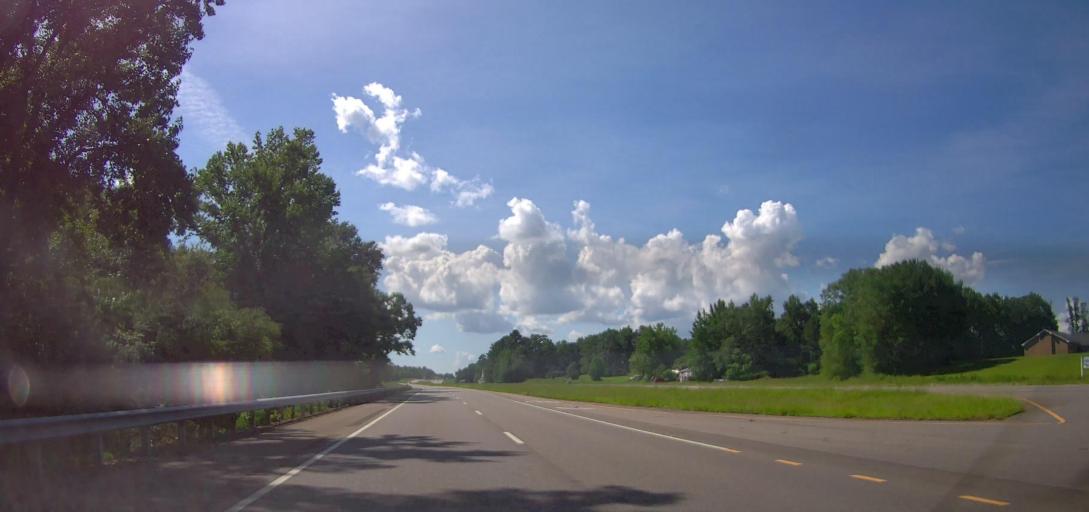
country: US
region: Alabama
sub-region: Pickens County
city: Gordo
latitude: 33.3485
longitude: -87.9537
